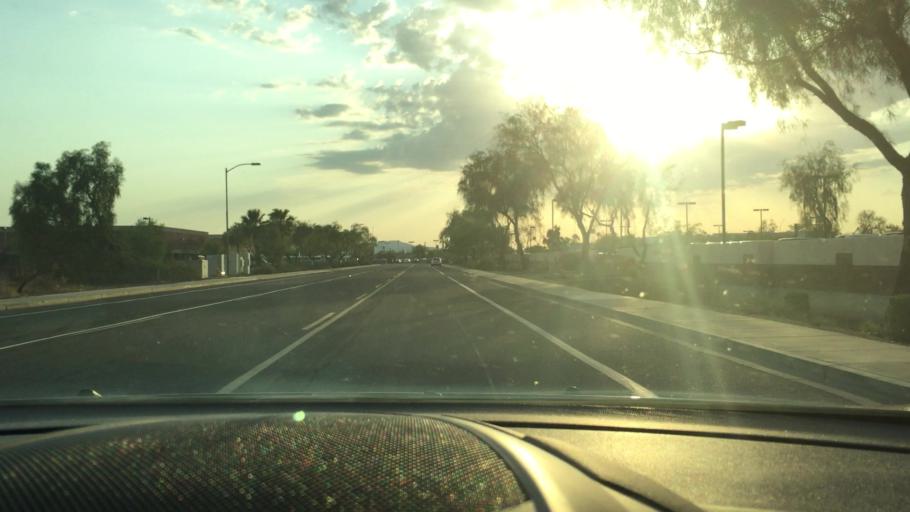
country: US
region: Arizona
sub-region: Maricopa County
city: Sun City
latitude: 33.6354
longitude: -112.2500
